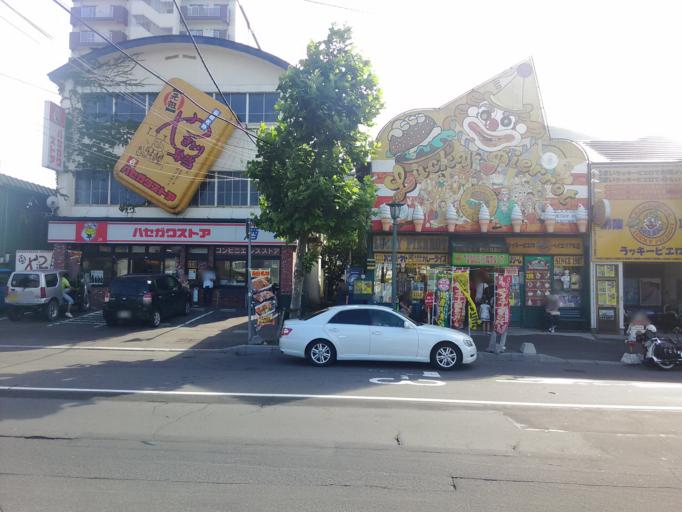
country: JP
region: Hokkaido
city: Hakodate
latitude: 41.7658
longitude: 140.7150
